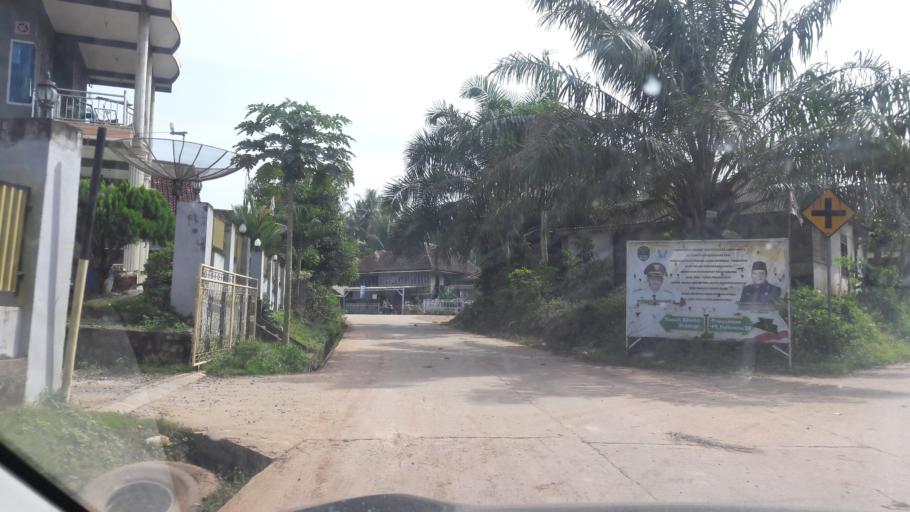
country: ID
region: South Sumatra
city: Gunungmenang
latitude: -3.3123
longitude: 104.1131
